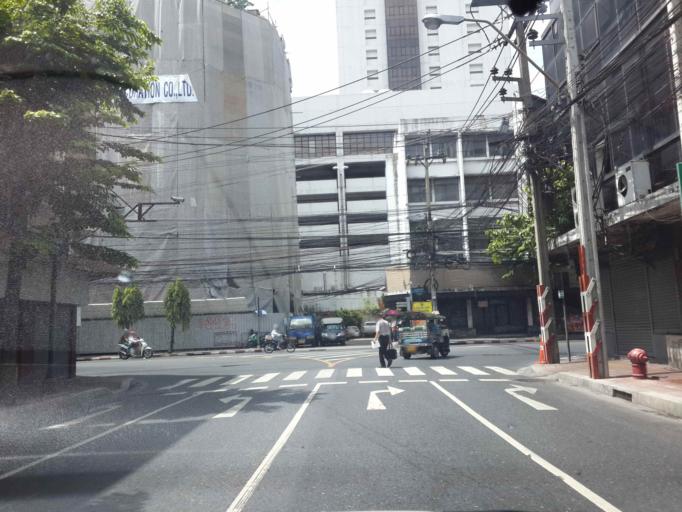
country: TH
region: Bangkok
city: Bang Rak
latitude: 13.7280
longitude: 100.5242
